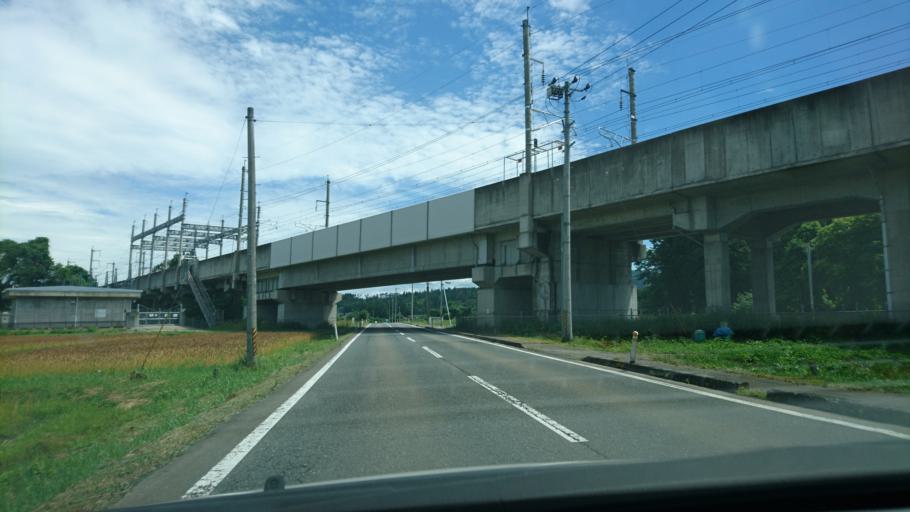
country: JP
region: Iwate
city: Hanamaki
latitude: 39.4219
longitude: 141.1772
